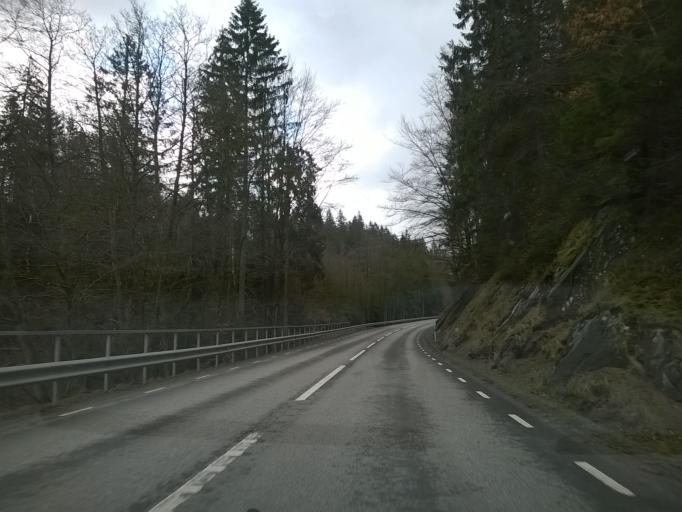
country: SE
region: Halland
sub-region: Varbergs Kommun
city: Tvaaker
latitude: 57.1516
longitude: 12.5917
